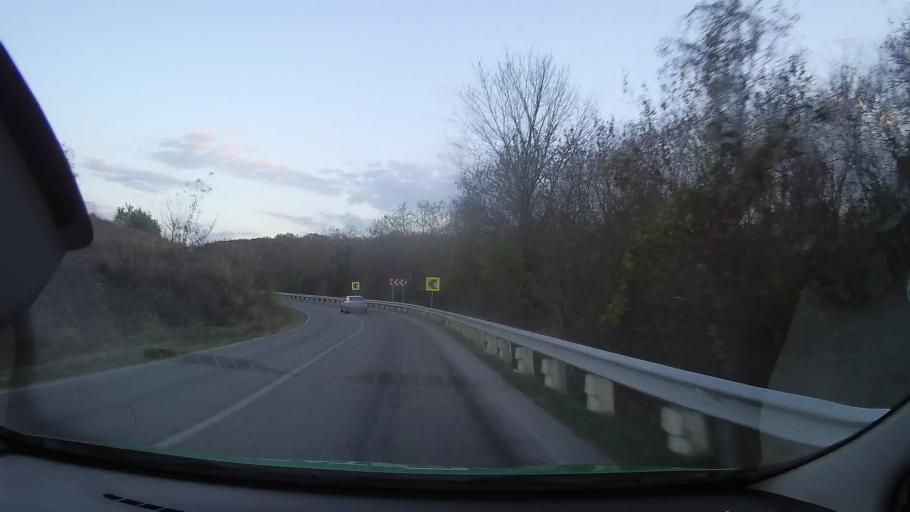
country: RO
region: Constanta
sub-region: Comuna Baneasa
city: Baneasa
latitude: 44.0770
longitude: 27.6683
